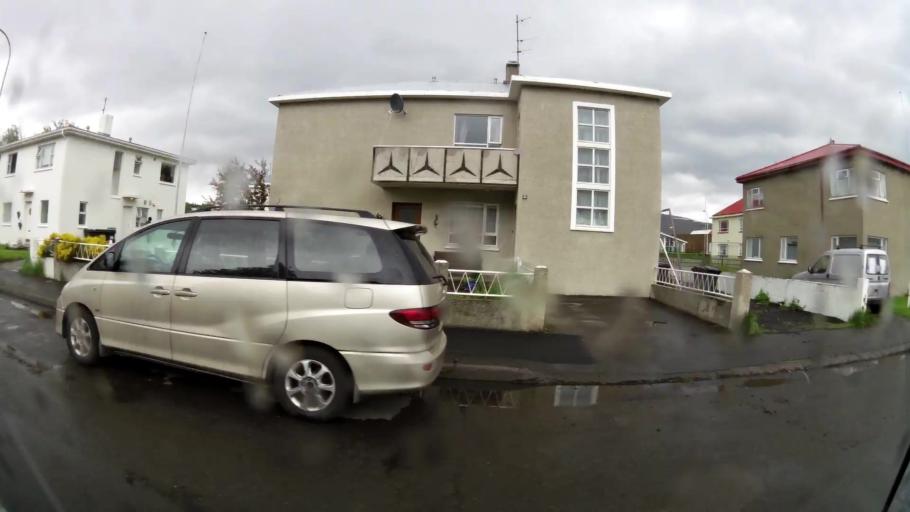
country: IS
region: Northeast
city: Akureyri
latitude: 65.6890
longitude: -18.0899
